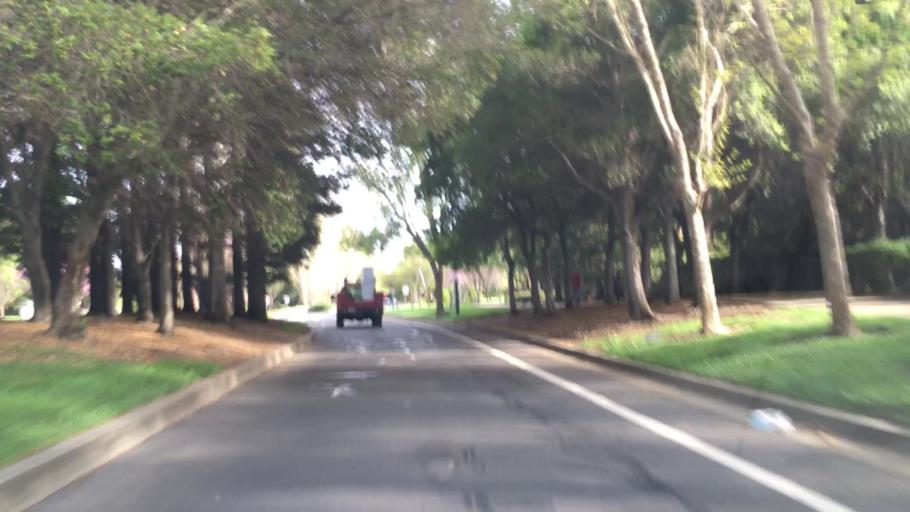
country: US
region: California
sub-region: Solano County
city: Green Valley
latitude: 38.2274
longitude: -122.1479
